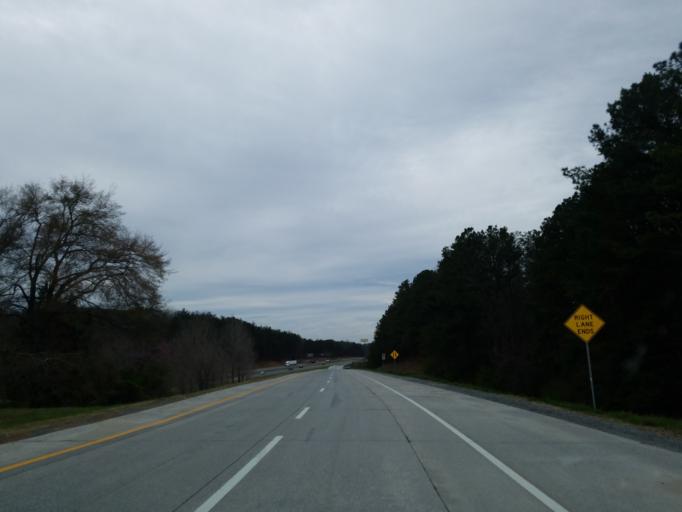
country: US
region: Georgia
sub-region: Bartow County
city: Emerson
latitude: 34.1434
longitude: -84.7376
